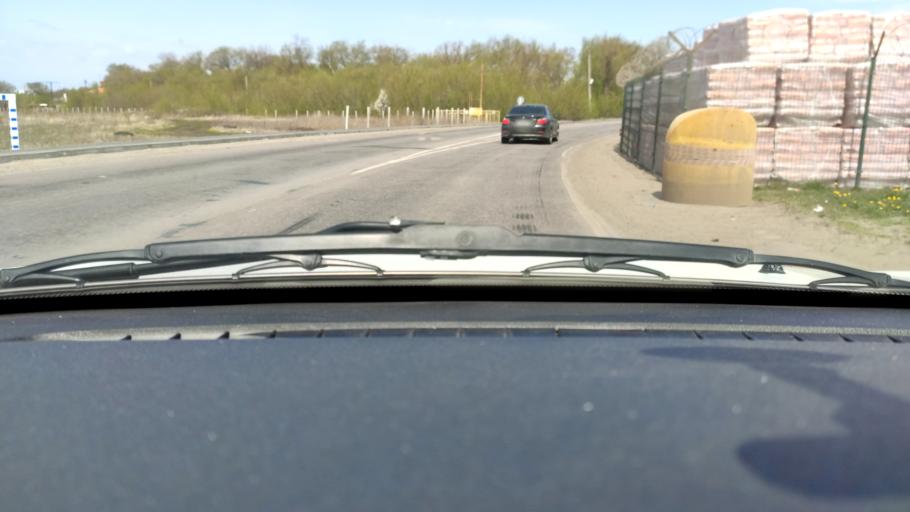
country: RU
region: Voronezj
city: Novaya Usman'
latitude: 51.6335
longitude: 39.3329
